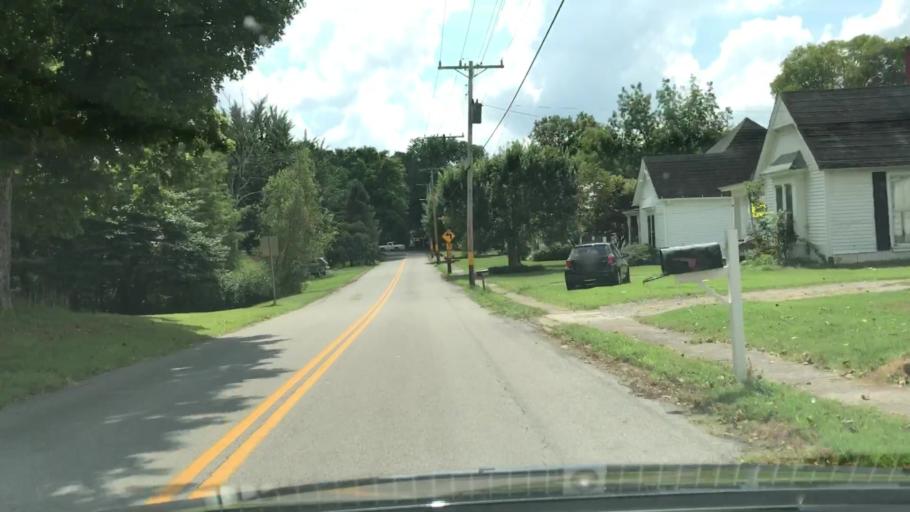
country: US
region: Kentucky
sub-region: Todd County
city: Guthrie
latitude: 36.7156
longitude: -87.0663
